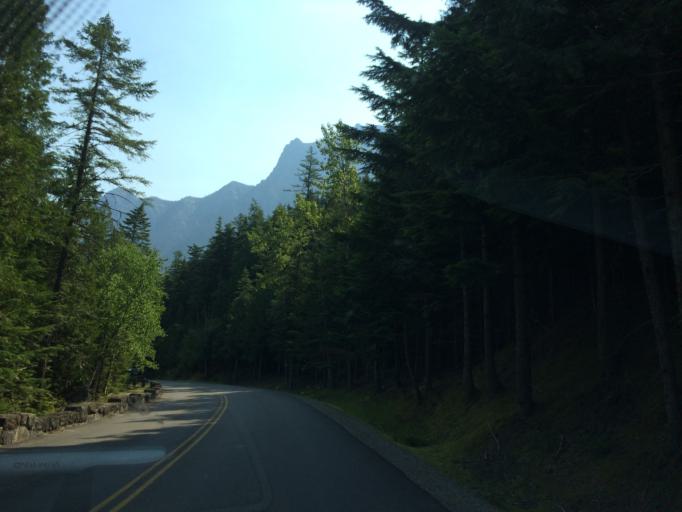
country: US
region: Montana
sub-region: Flathead County
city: Columbia Falls
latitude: 48.6409
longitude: -113.8584
